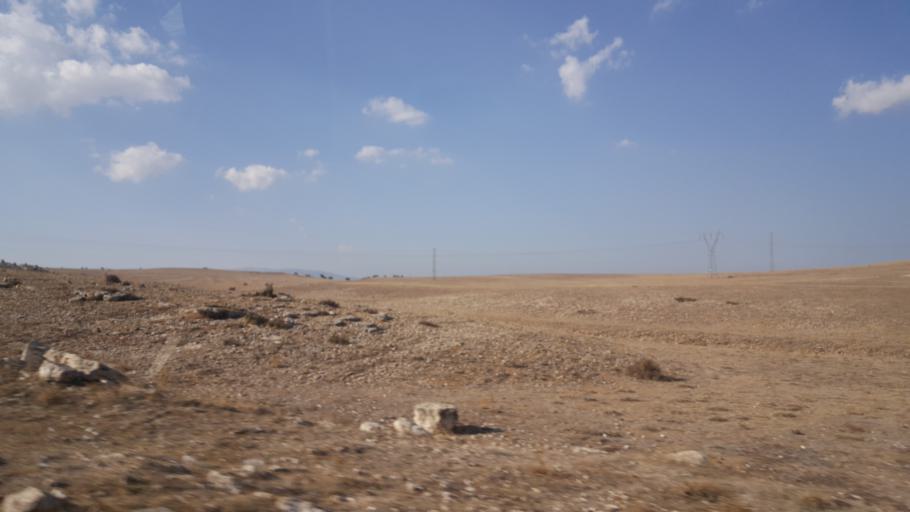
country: TR
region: Eskisehir
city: Kirka
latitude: 39.3211
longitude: 30.5563
